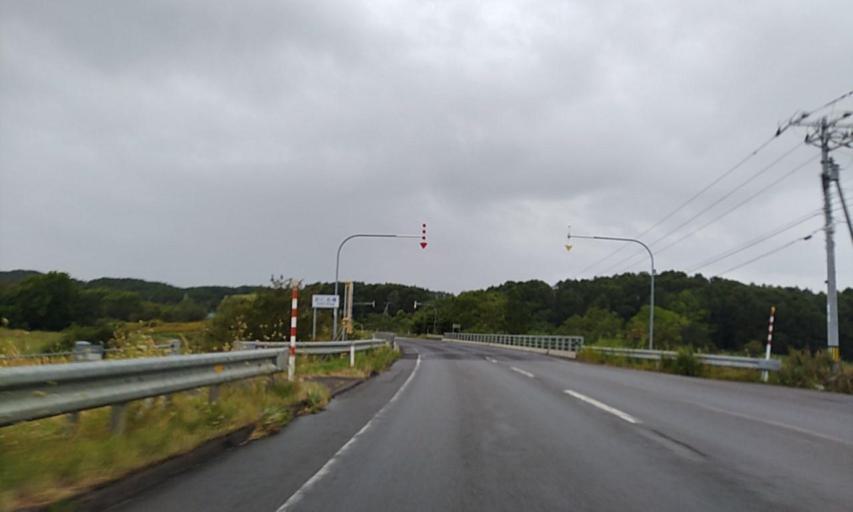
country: JP
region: Hokkaido
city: Mombetsu
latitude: 44.5018
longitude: 143.0714
